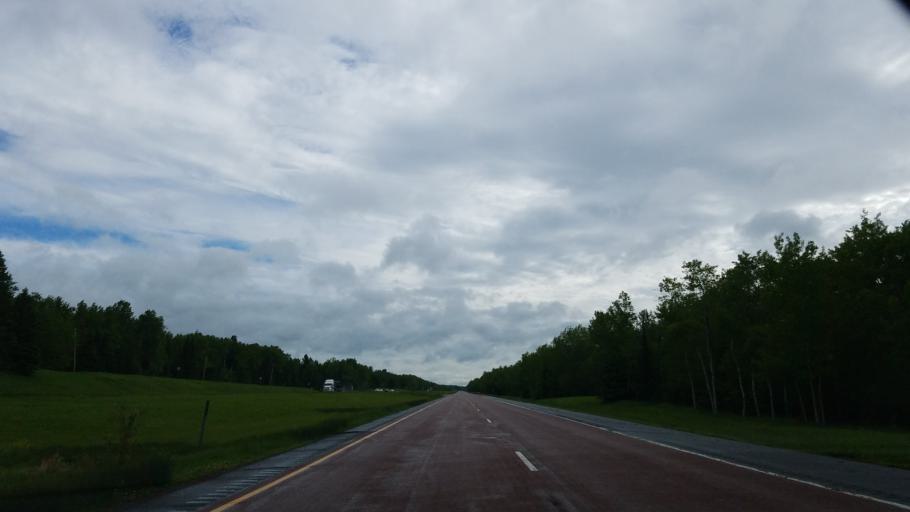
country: US
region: Minnesota
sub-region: Saint Louis County
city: Arnold
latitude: 46.8698
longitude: -91.9557
